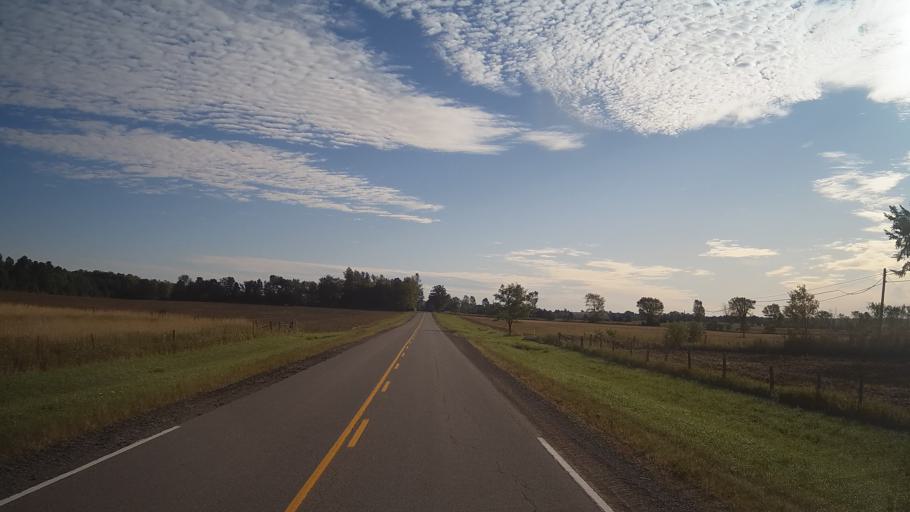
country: CA
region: Ontario
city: Gananoque
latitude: 44.3918
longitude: -76.1208
